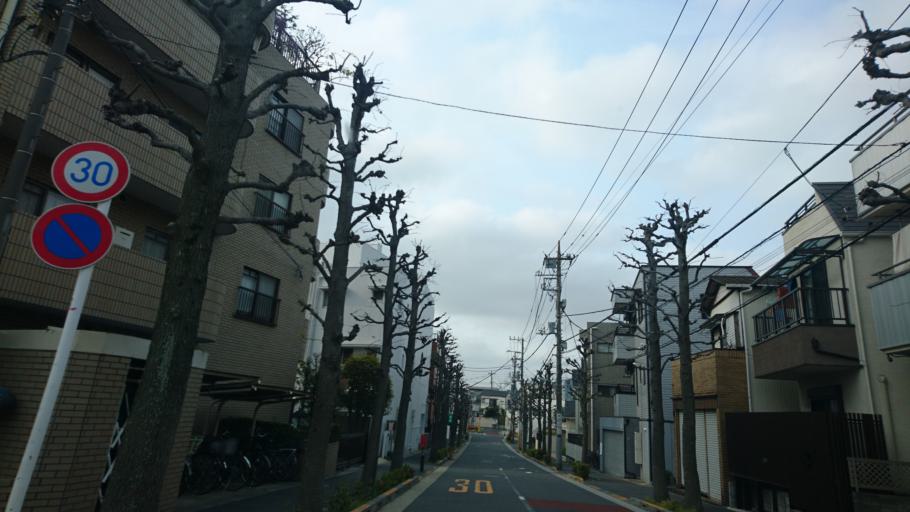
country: JP
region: Kanagawa
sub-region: Kawasaki-shi
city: Kawasaki
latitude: 35.5977
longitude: 139.7251
